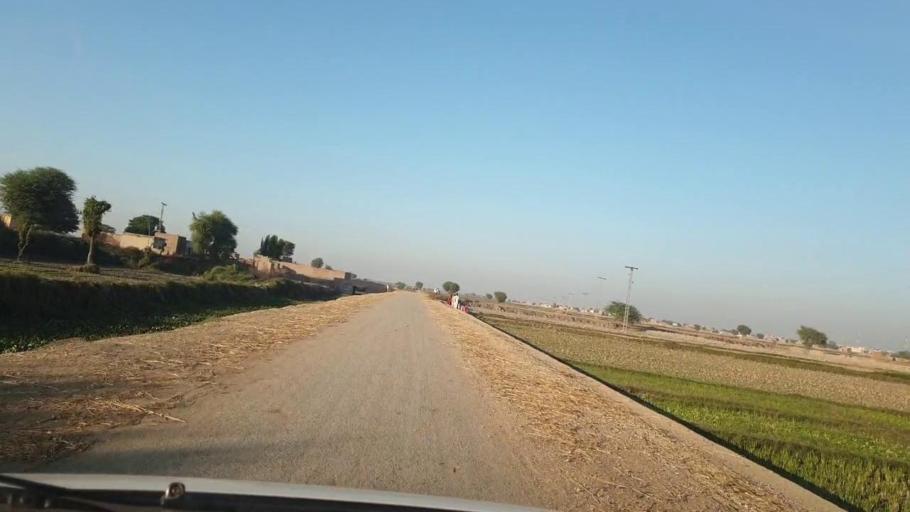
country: PK
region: Sindh
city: Khairpur Nathan Shah
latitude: 27.0721
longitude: 67.7220
